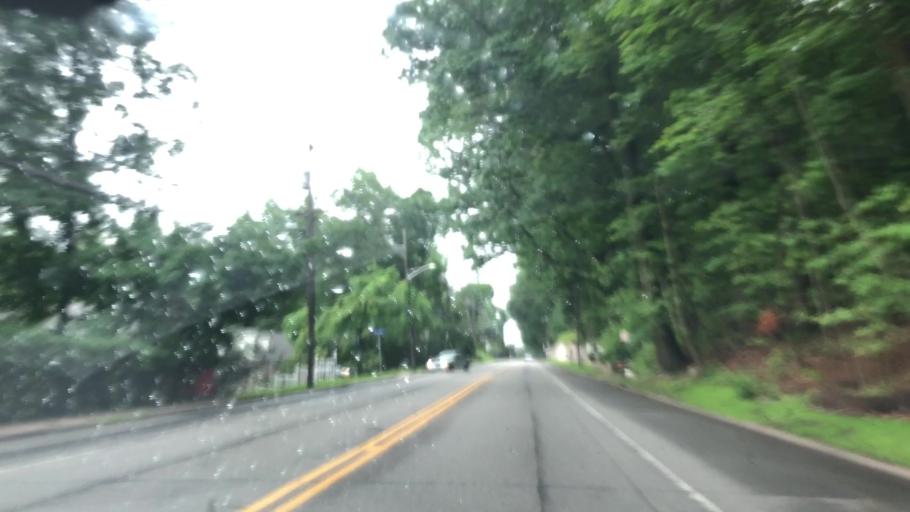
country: US
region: New Jersey
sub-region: Passaic County
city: Little Falls
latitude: 40.8662
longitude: -74.1922
